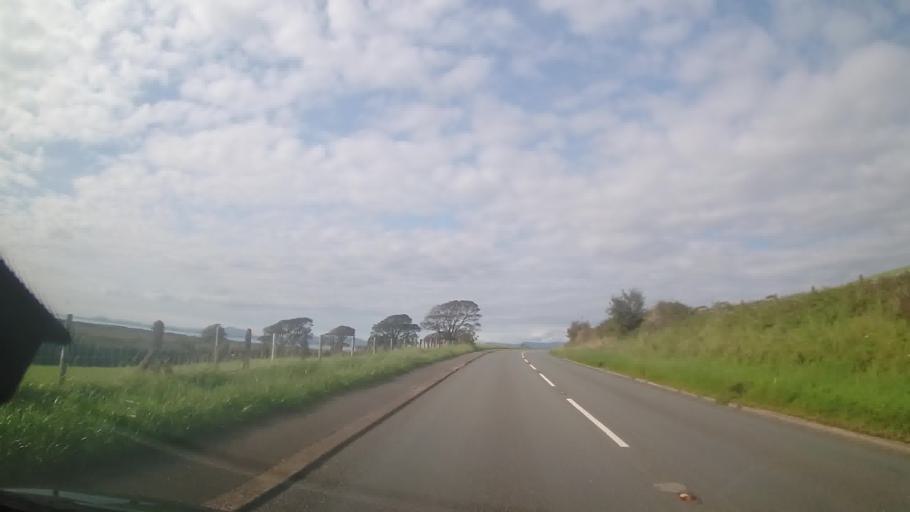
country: GB
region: Wales
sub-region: Gwynedd
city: Llanbedr
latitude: 52.8025
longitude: -4.1014
